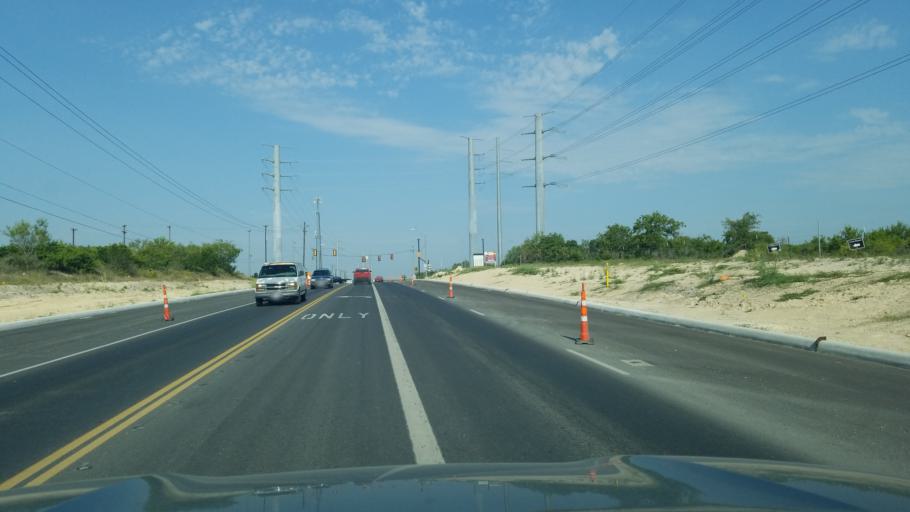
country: US
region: Texas
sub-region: Medina County
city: La Coste
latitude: 29.4213
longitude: -98.7809
